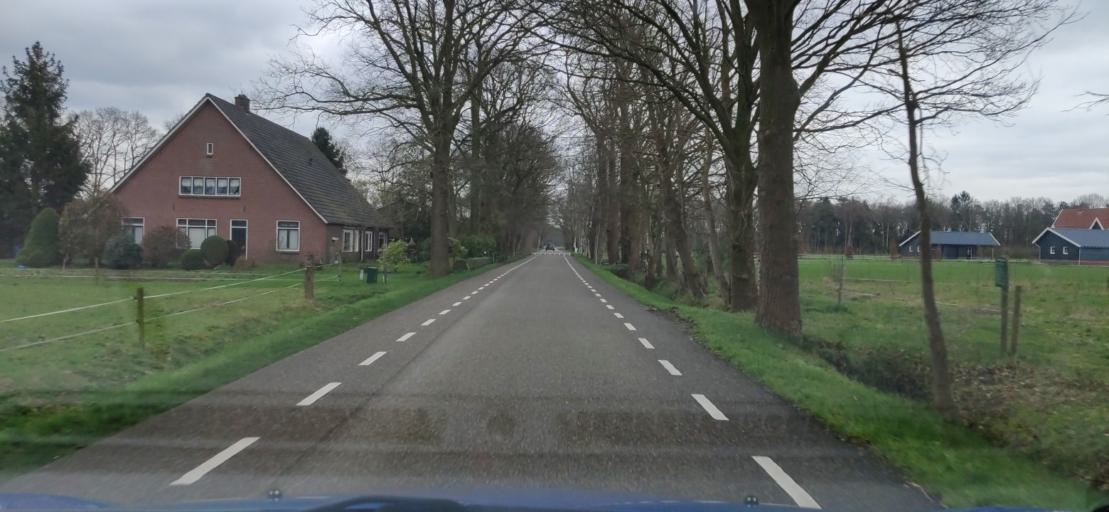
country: NL
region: Overijssel
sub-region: Gemeente Hengelo
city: Hengelo
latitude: 52.2309
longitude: 6.7617
